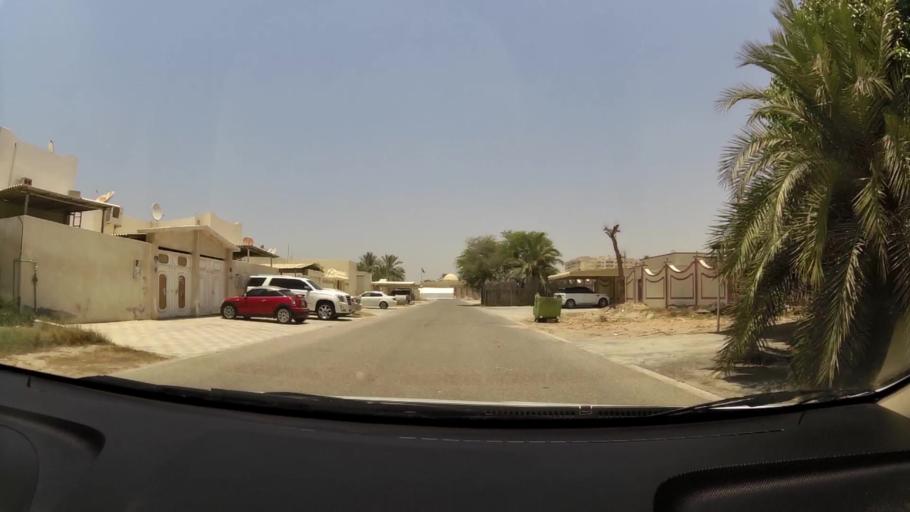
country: AE
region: Umm al Qaywayn
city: Umm al Qaywayn
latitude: 25.5383
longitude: 55.5370
